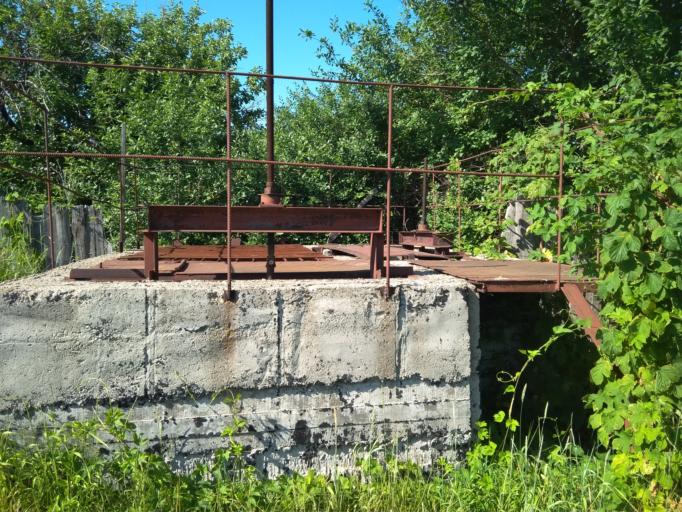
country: RU
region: Ulyanovsk
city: Novoul'yanovsk
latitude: 54.2371
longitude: 48.3457
